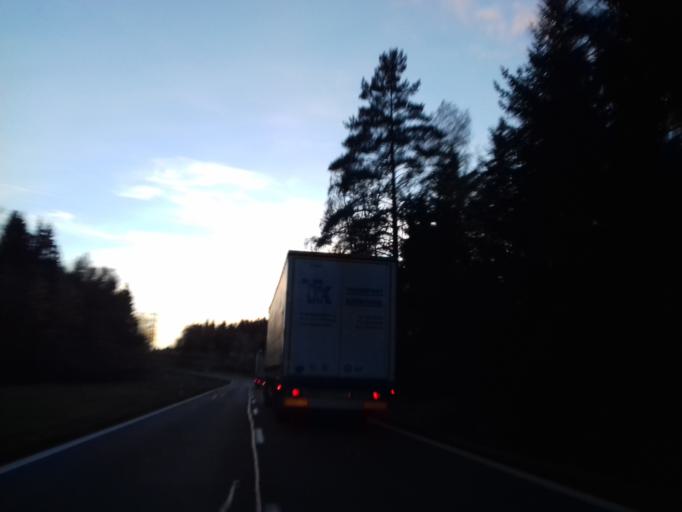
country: CZ
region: Vysocina
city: Krizova
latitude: 49.6878
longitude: 15.7897
